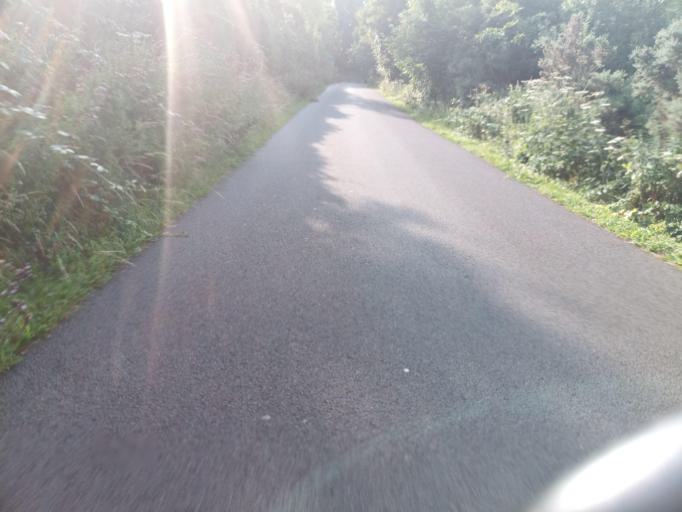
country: GB
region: Northern Ireland
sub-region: Castlereagh District
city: Dundonald
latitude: 54.5896
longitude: -5.8149
